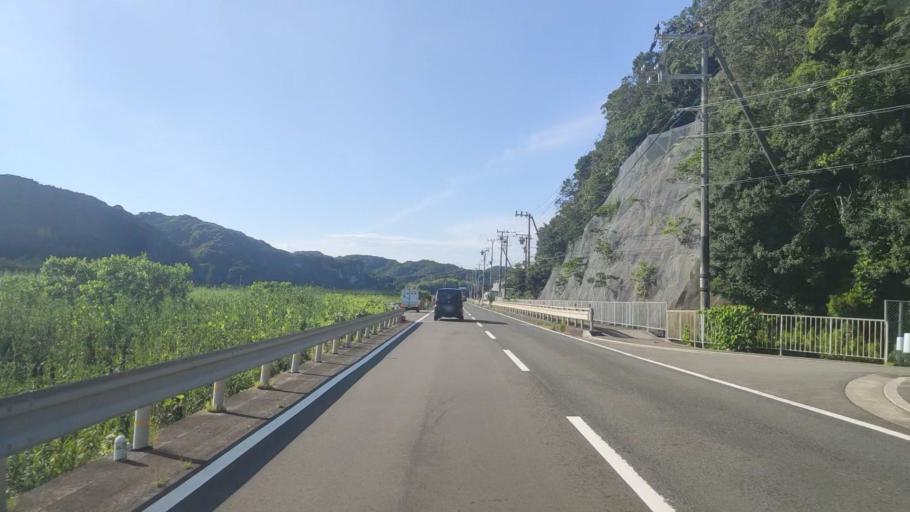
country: JP
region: Wakayama
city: Tanabe
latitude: 33.6574
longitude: 135.4012
